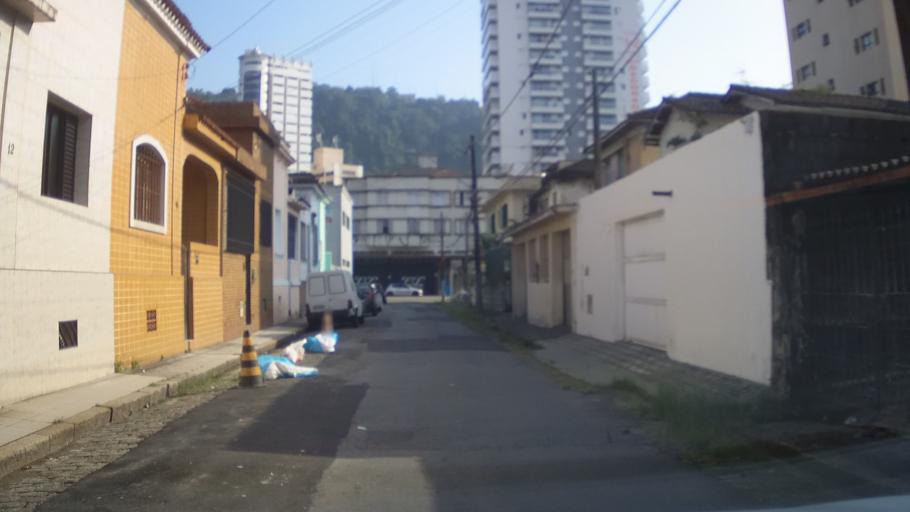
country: BR
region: Sao Paulo
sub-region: Santos
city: Santos
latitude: -23.9459
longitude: -46.3309
